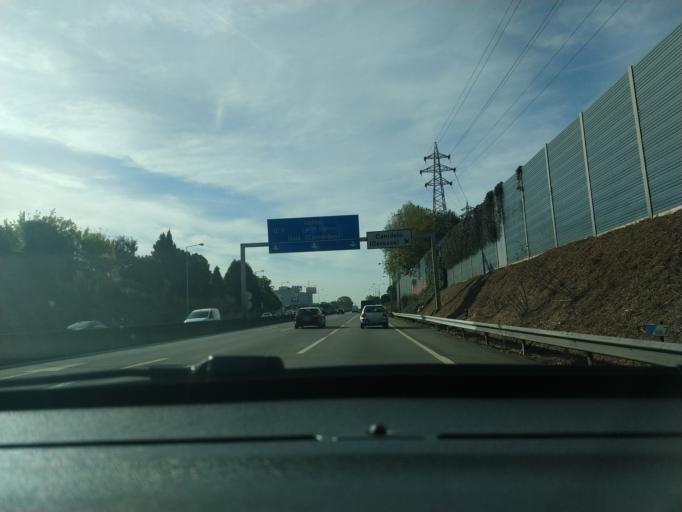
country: PT
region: Porto
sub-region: Vila Nova de Gaia
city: Canidelo
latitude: 41.1302
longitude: -8.6357
